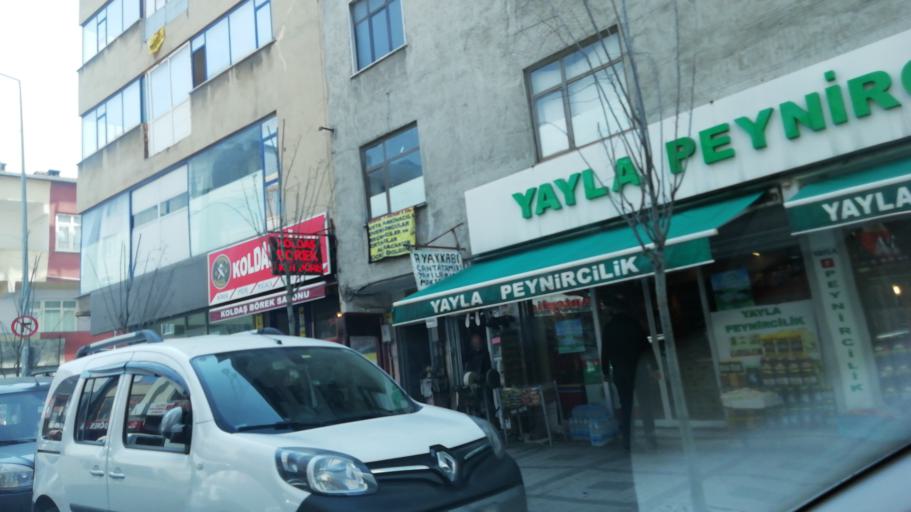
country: TR
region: Istanbul
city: Mahmutbey
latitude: 41.0334
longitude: 28.8201
